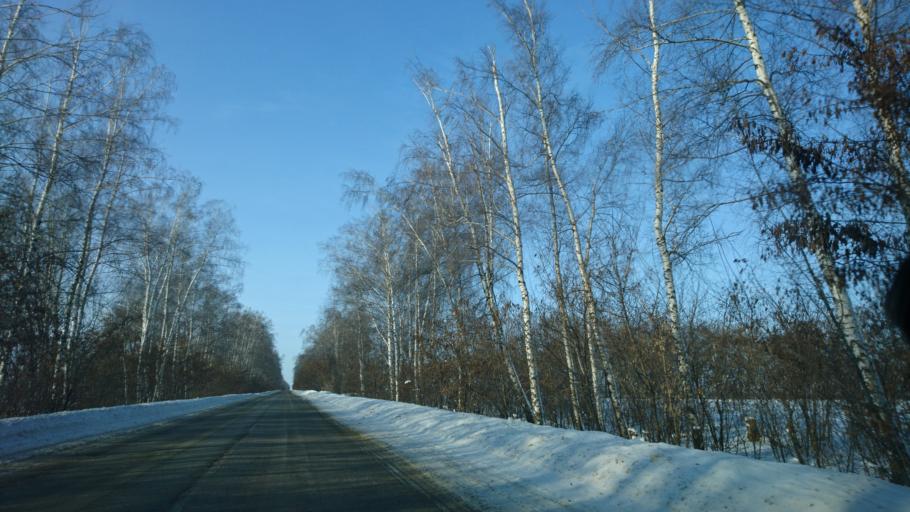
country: RU
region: Belgorod
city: Severnyy
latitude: 50.7274
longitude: 36.5519
